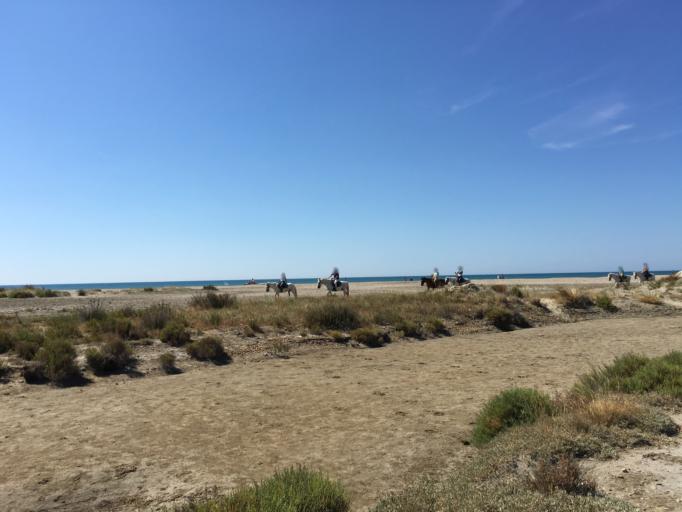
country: FR
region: Provence-Alpes-Cote d'Azur
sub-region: Departement des Bouches-du-Rhone
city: Saintes-Maries-de-la-Mer
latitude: 43.4585
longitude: 4.4350
